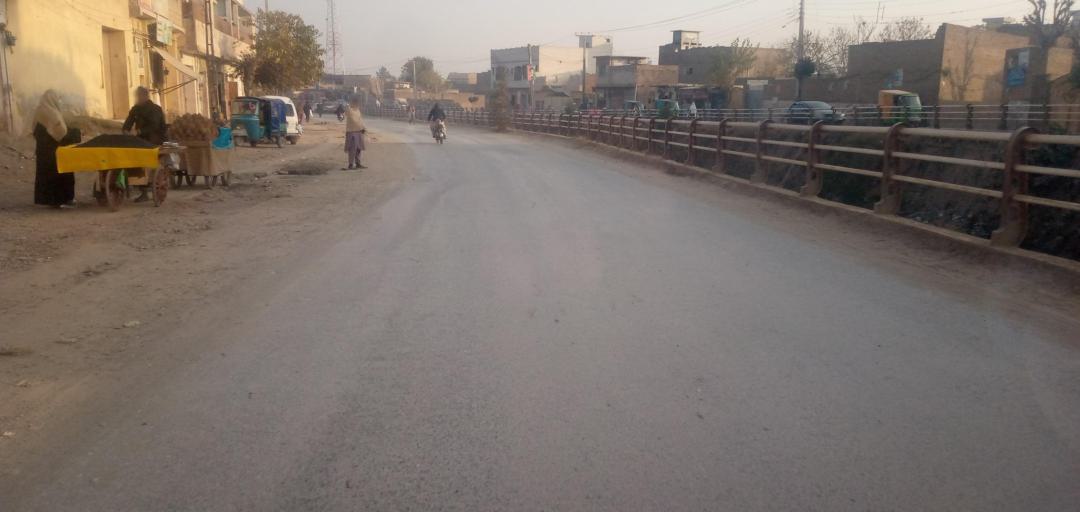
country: PK
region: Khyber Pakhtunkhwa
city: Peshawar
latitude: 33.9737
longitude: 71.5195
